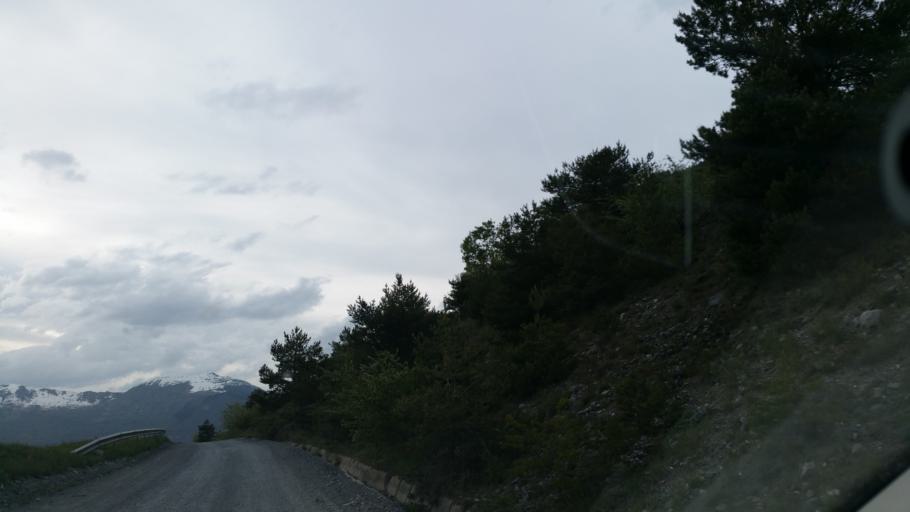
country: FR
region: Rhone-Alpes
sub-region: Departement de la Savoie
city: Saint-Michel-de-Maurienne
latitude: 45.2460
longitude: 6.4302
